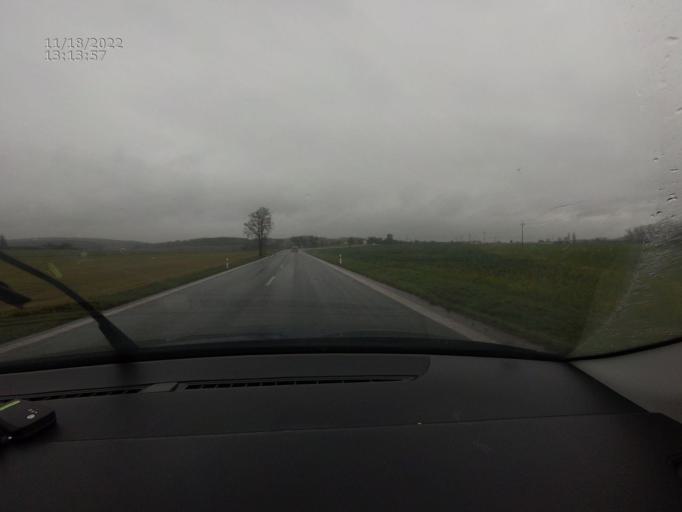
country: CZ
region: Plzensky
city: Horazd'ovice
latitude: 49.3265
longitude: 13.6381
